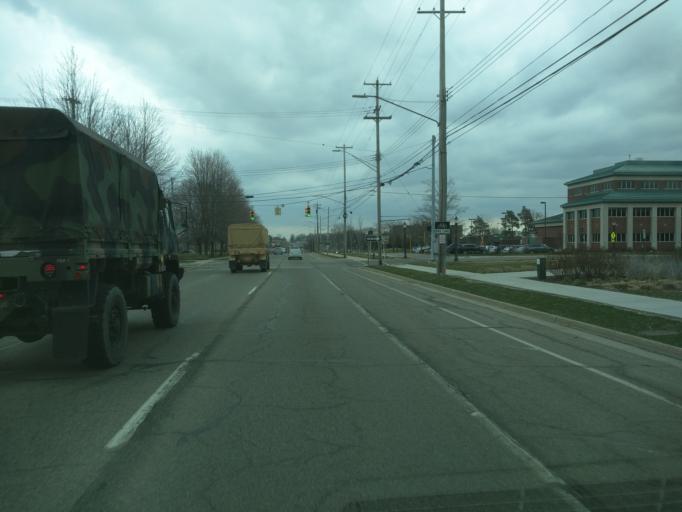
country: US
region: Michigan
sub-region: Ingham County
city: Lansing
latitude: 42.7409
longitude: -84.5546
